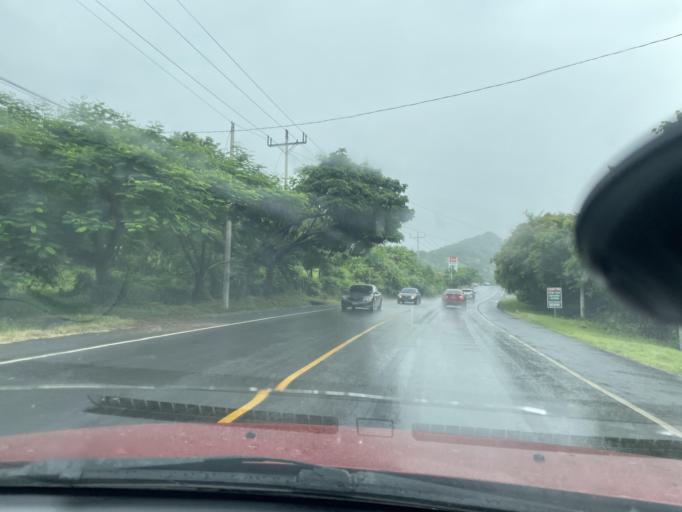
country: SV
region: Morazan
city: Jocoro
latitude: 13.5666
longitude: -88.0939
